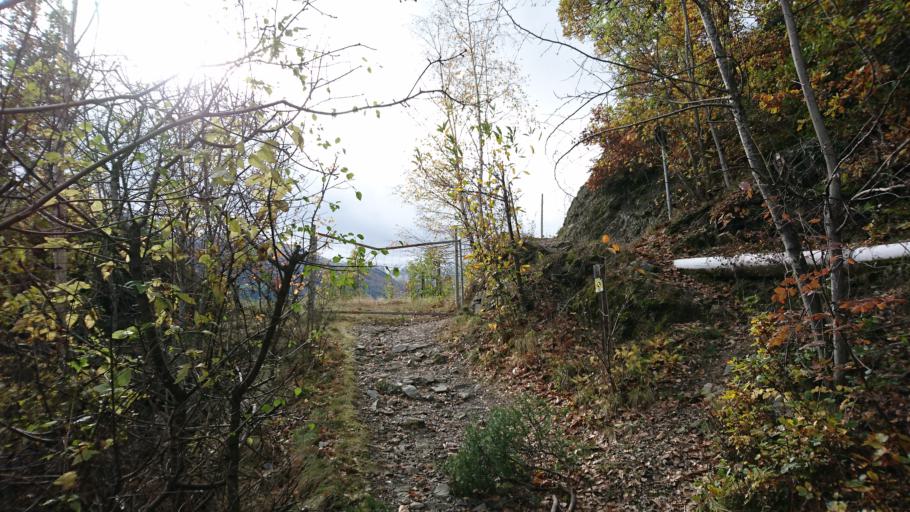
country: IT
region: Trentino-Alto Adige
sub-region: Bolzano
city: Naturno
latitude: 46.6581
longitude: 11.0128
